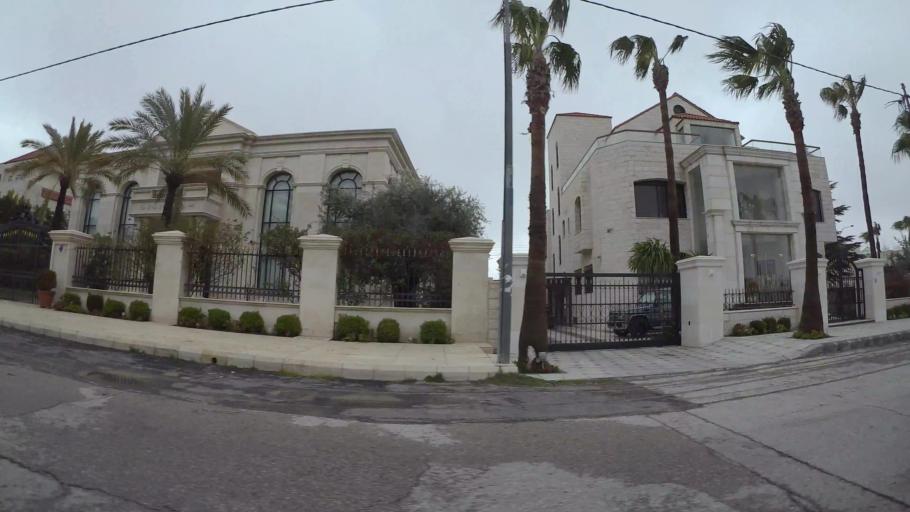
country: JO
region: Amman
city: Al Bunayyat ash Shamaliyah
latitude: 31.9437
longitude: 35.8765
